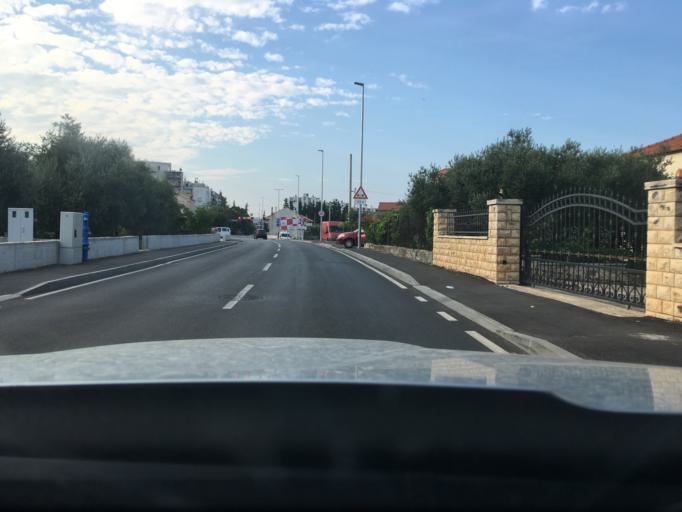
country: HR
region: Zadarska
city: Zadar
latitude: 44.1276
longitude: 15.2330
